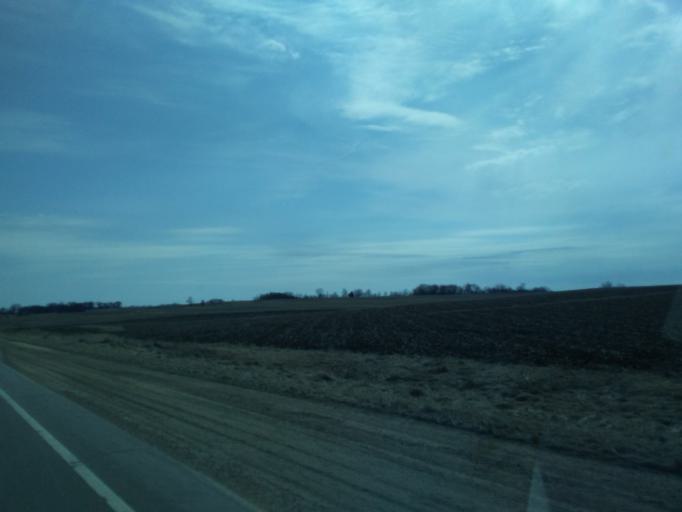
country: US
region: Iowa
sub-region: Winneshiek County
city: Decorah
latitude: 43.4104
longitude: -91.8568
